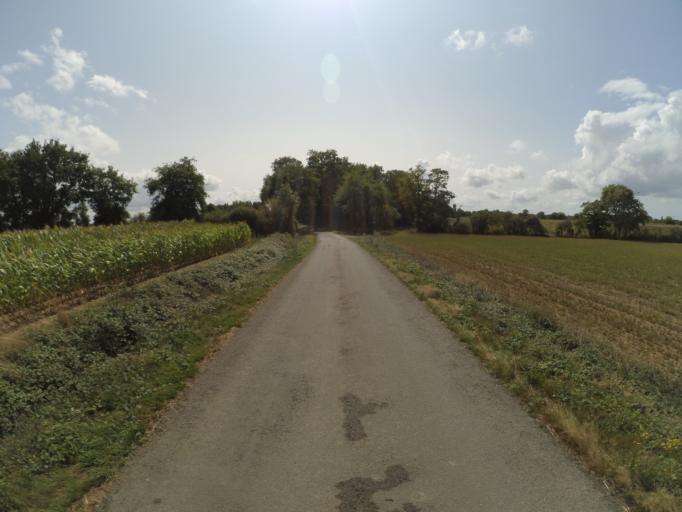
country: FR
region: Pays de la Loire
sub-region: Departement de la Vendee
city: La Bernardiere
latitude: 47.0270
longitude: -1.2515
